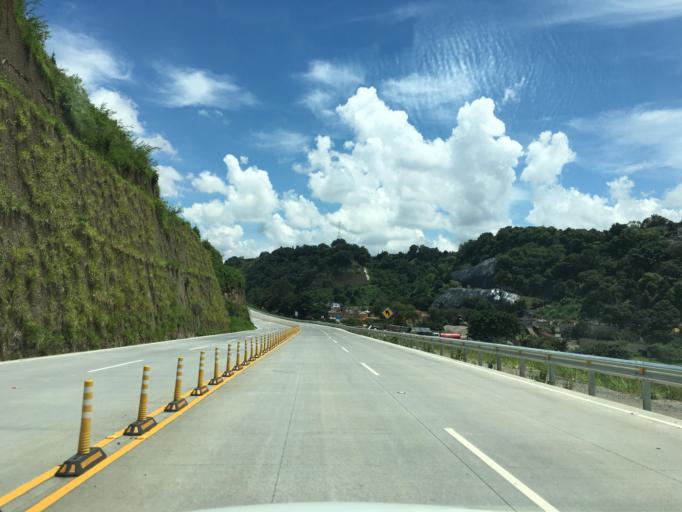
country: GT
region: Guatemala
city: Petapa
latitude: 14.5428
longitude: -90.5339
